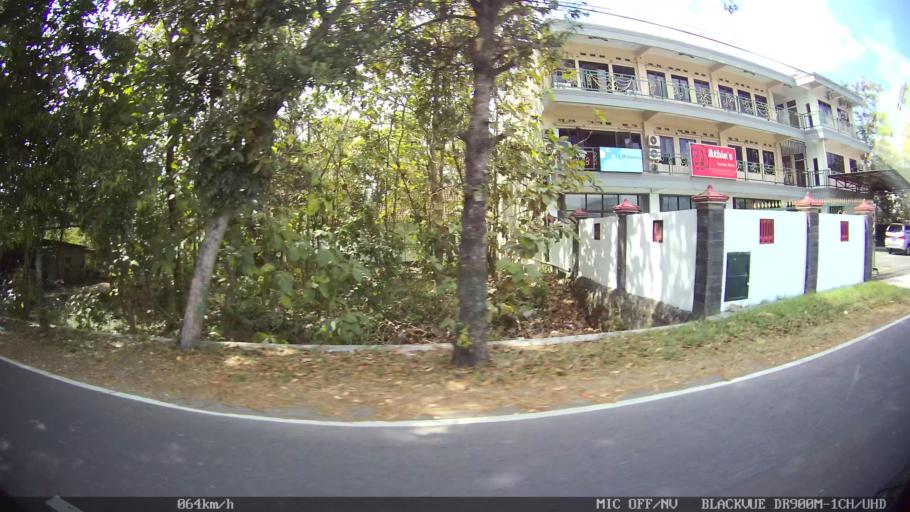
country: ID
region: Daerah Istimewa Yogyakarta
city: Srandakan
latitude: -7.8759
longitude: 110.1348
